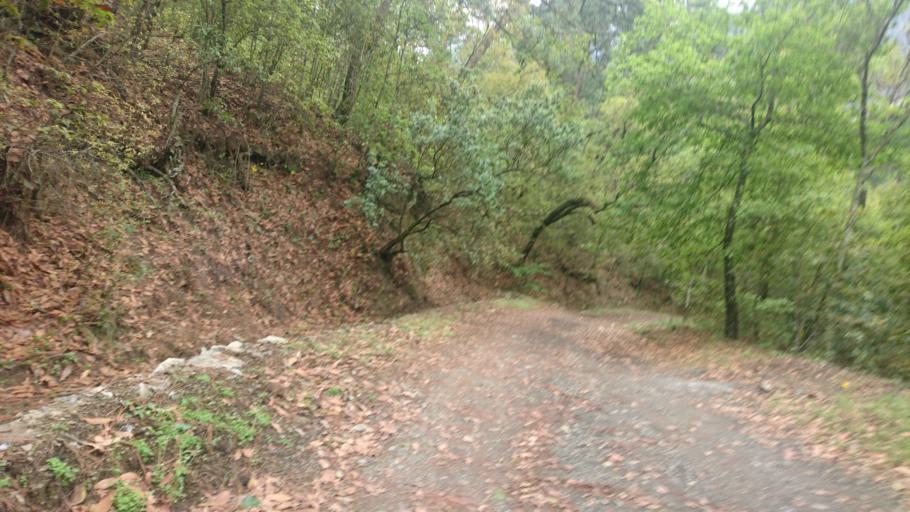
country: MX
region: Nuevo Leon
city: Garza Garcia
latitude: 25.6058
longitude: -100.3440
